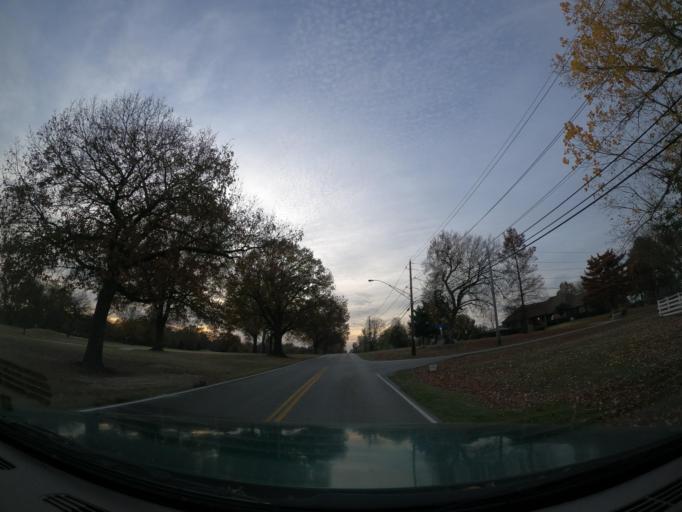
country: US
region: Oklahoma
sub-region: Tulsa County
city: Broken Arrow
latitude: 35.9739
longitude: -95.8046
